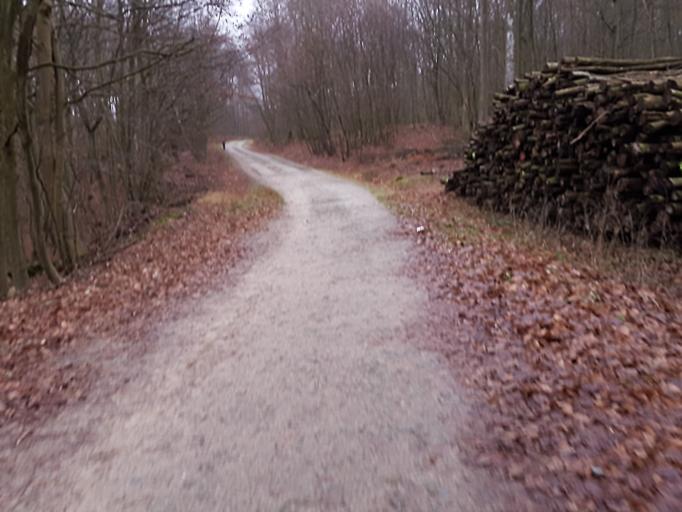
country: DE
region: Mecklenburg-Vorpommern
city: Ostseebad Binz
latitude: 54.3974
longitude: 13.6357
